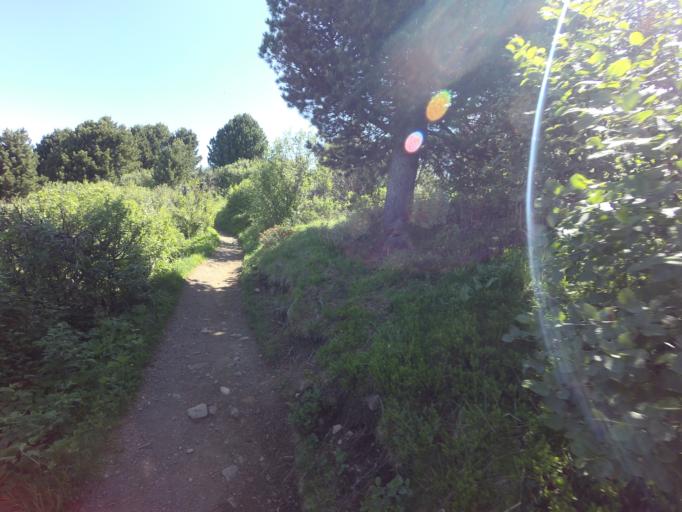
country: IT
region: Trentino-Alto Adige
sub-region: Bolzano
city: Castelrotto
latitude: 46.5586
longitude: 11.6034
